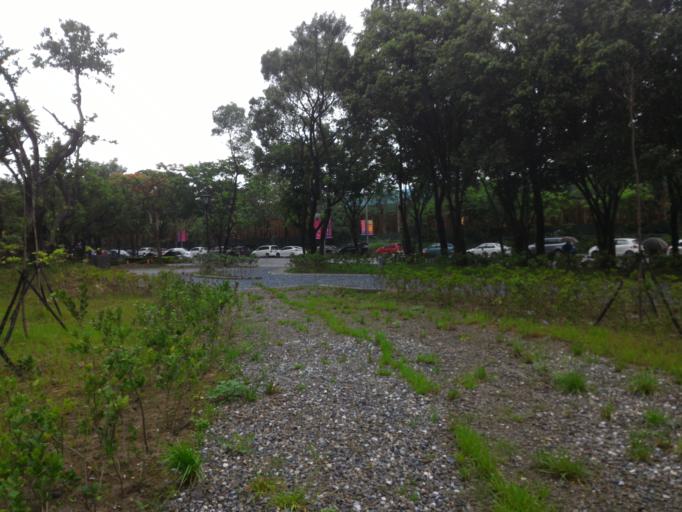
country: TW
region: Taiwan
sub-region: Taoyuan
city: Taoyuan
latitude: 24.9490
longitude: 121.3753
